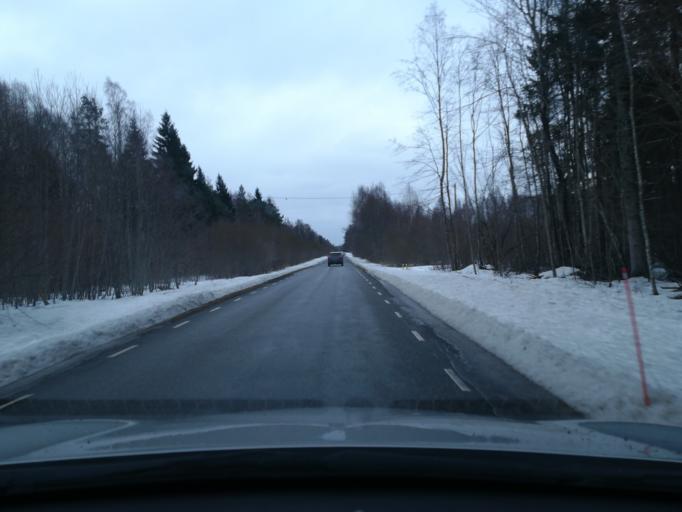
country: EE
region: Harju
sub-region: Nissi vald
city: Turba
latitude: 59.0687
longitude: 24.2508
